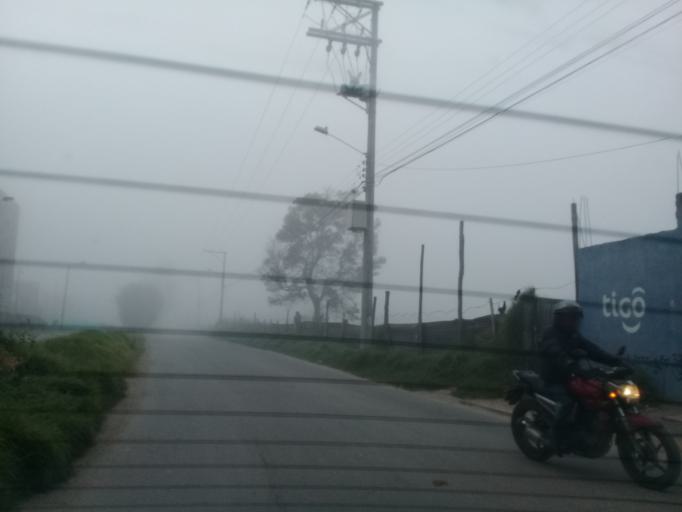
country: CO
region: Cundinamarca
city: Madrid
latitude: 4.7342
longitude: -74.2514
